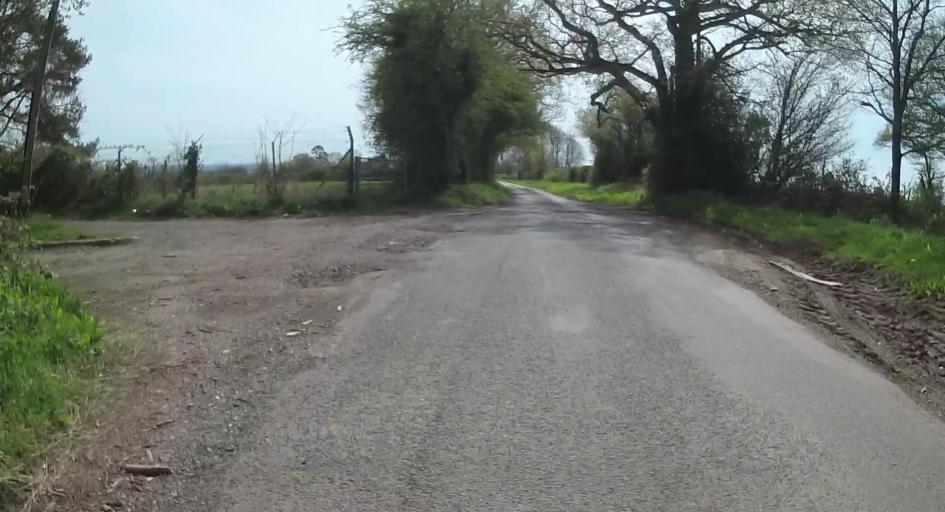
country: GB
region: England
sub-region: Hampshire
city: Alton
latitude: 51.1824
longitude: -0.9686
